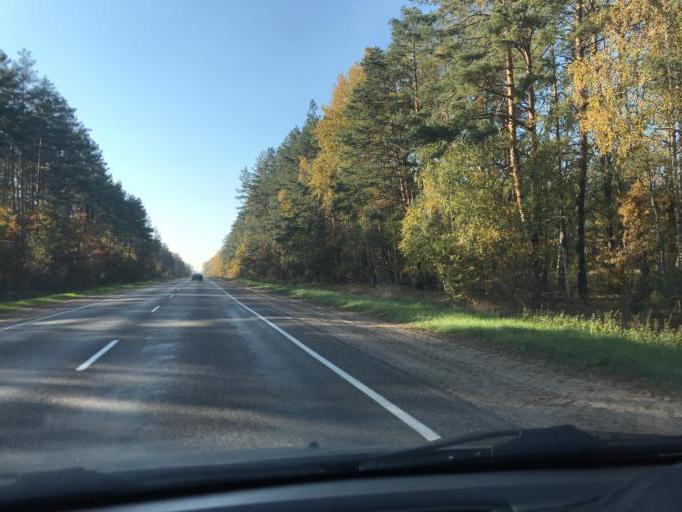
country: BY
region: Mogilev
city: Hlusha
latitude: 53.0945
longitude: 28.9616
